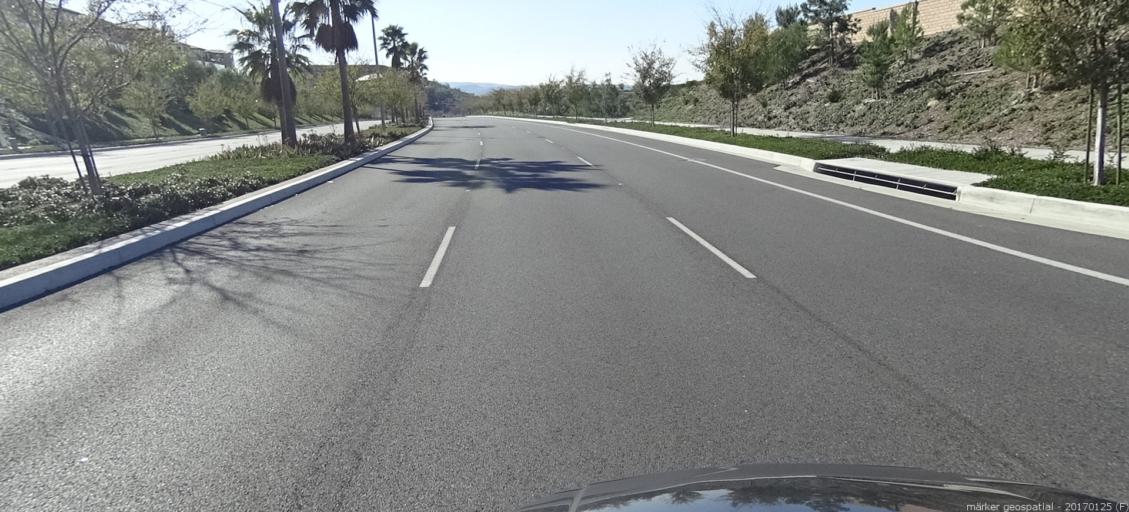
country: US
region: California
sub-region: Orange County
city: Lake Forest
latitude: 33.6716
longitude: -117.6868
